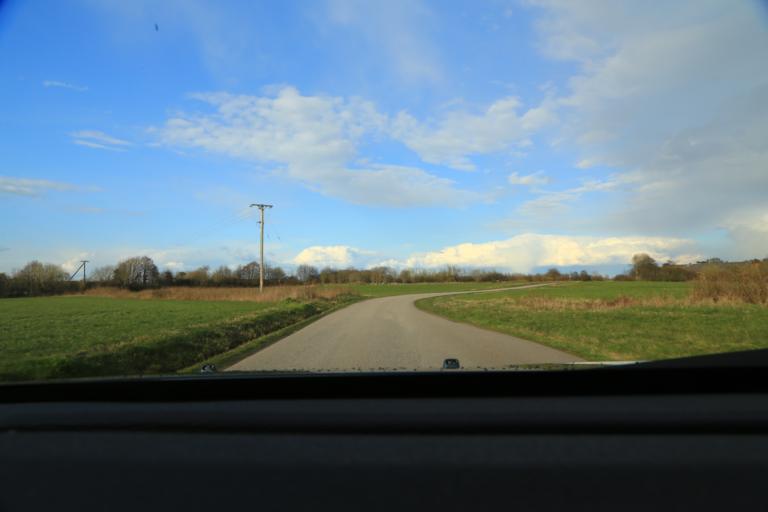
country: SE
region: Halland
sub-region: Varbergs Kommun
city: Traslovslage
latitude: 57.0503
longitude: 12.2979
